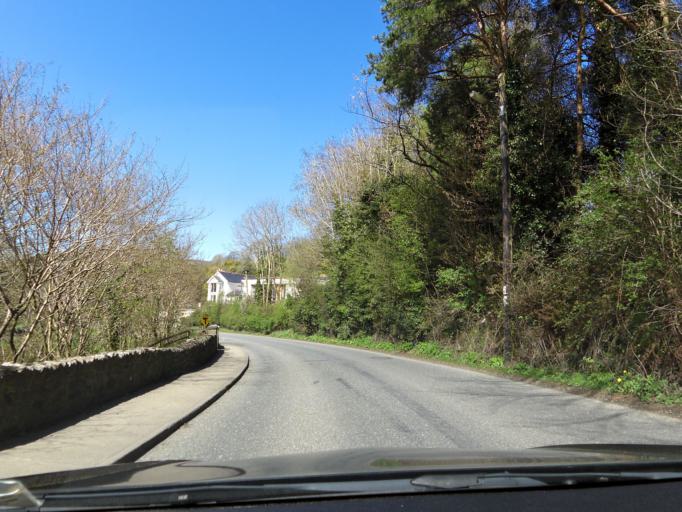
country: IE
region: Leinster
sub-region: Wicklow
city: Carnew
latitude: 52.7989
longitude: -6.4608
